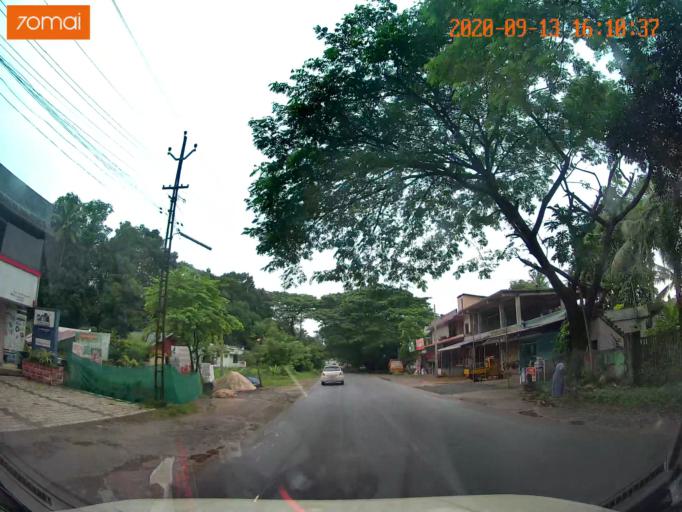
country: IN
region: Kerala
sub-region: Kottayam
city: Palackattumala
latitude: 9.6820
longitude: 76.6077
